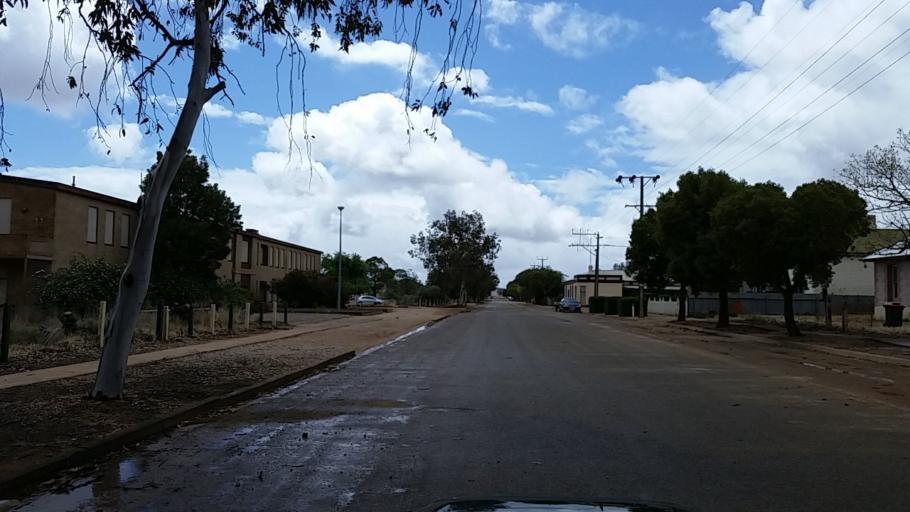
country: AU
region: South Australia
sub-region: Peterborough
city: Peterborough
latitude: -32.9747
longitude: 138.8360
